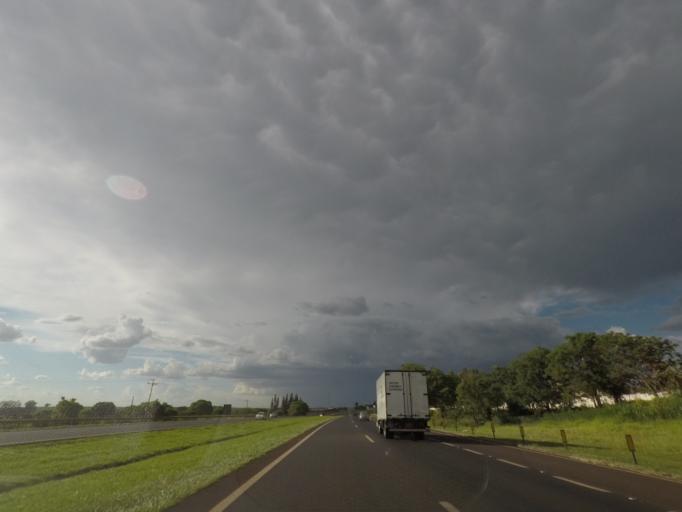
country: BR
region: Sao Paulo
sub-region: Jardinopolis
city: Jardinopolis
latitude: -21.0564
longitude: -47.8221
